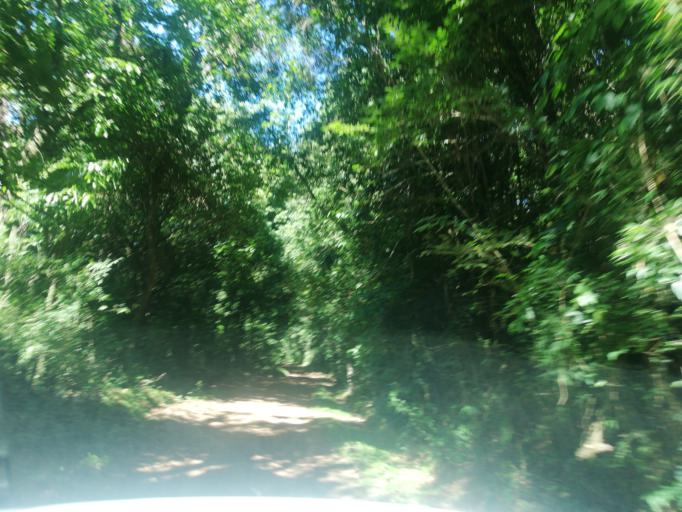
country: AR
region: Misiones
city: Cerro Azul
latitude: -27.7420
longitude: -55.5712
